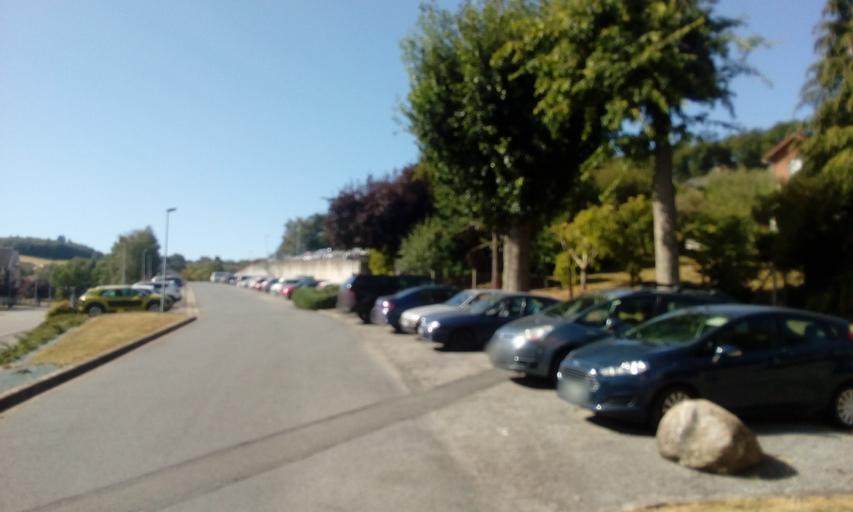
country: FR
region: Limousin
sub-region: Departement de la Creuse
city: Gueret
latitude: 46.1648
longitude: 1.8729
